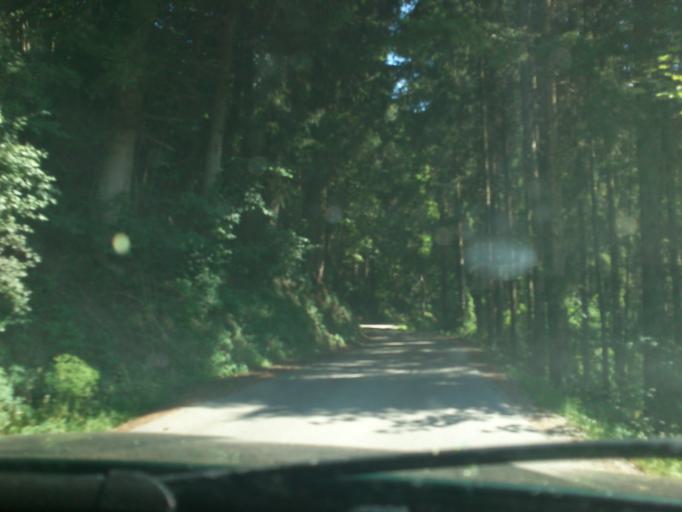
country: AT
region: Upper Austria
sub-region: Politischer Bezirk Kirchdorf an der Krems
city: Rossleithen
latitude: 47.7195
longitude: 14.3554
